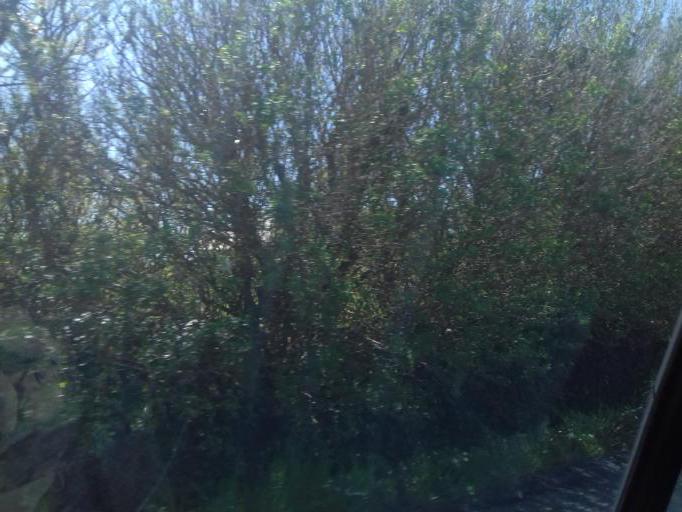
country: IE
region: Munster
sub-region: Waterford
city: Dunmore East
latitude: 52.1365
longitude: -6.9208
